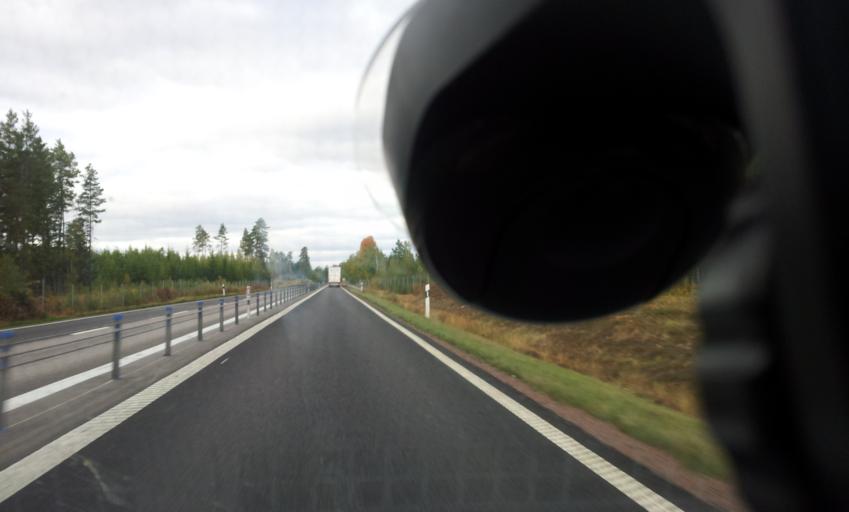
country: SE
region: Kalmar
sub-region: Monsteras Kommun
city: Timmernabben
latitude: 56.8771
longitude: 16.3826
